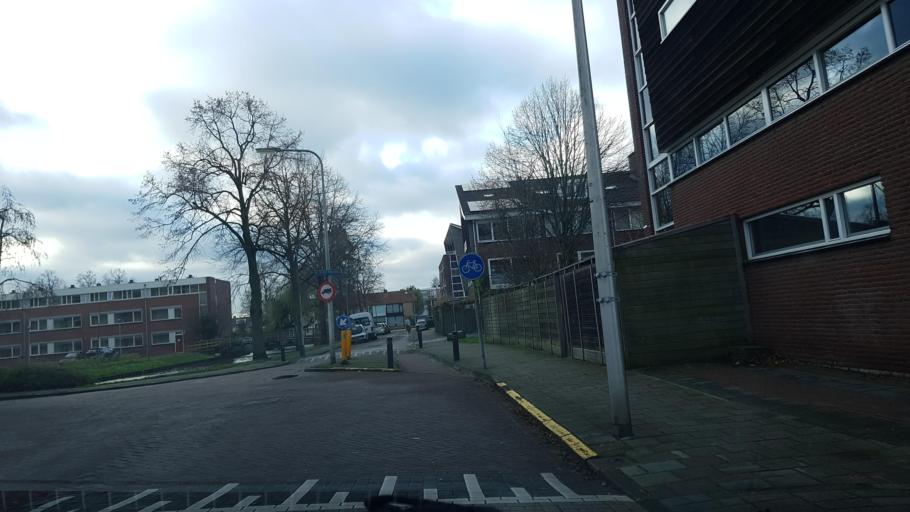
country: NL
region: South Holland
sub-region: Bodegraven-Reeuwijk
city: Bodegraven
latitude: 52.0805
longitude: 4.7421
